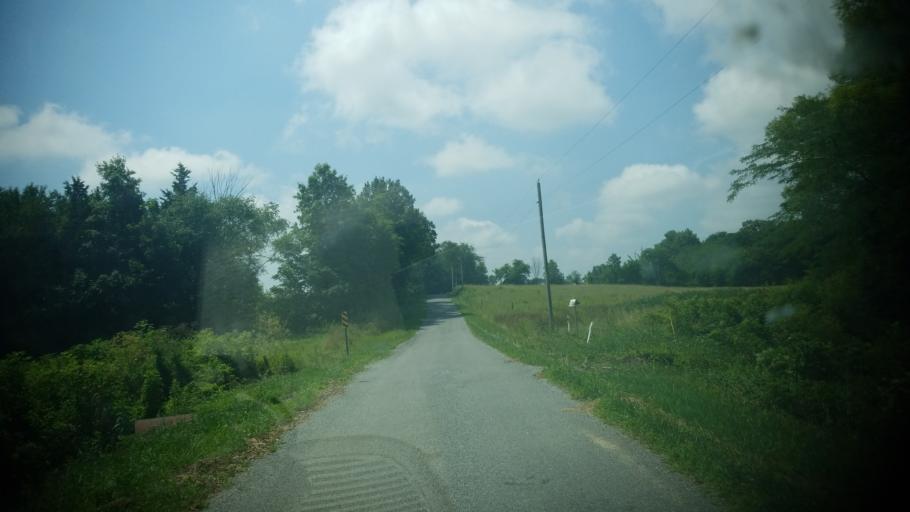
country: US
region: Illinois
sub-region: Wayne County
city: Fairfield
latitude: 38.5242
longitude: -88.3655
